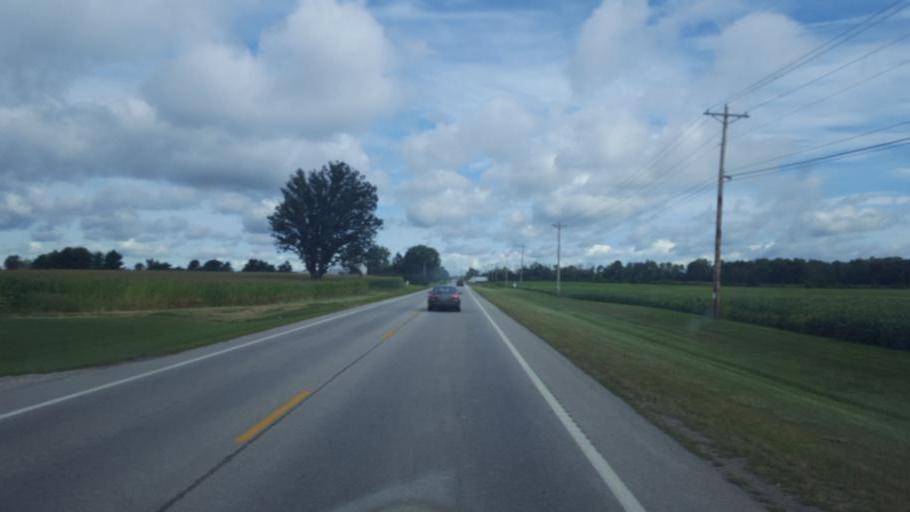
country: US
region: Ohio
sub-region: Lorain County
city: Oberlin
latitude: 41.2420
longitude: -82.2181
